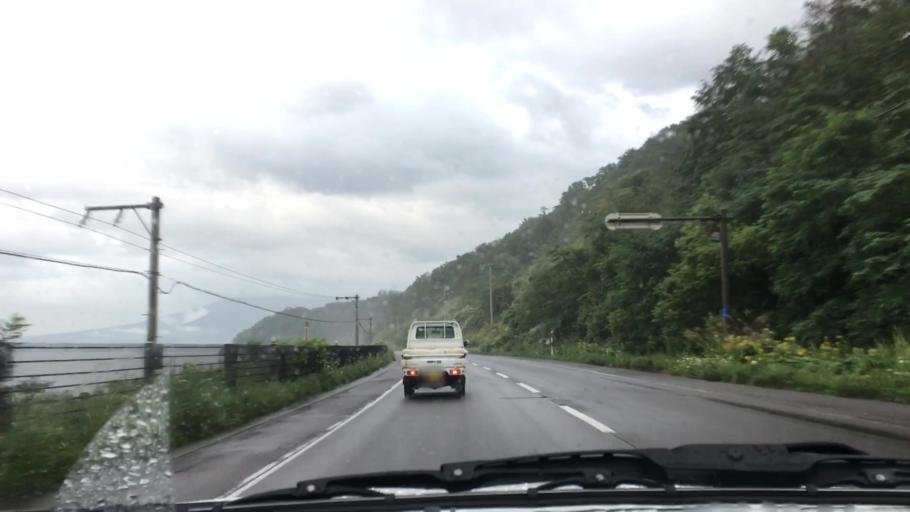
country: JP
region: Hokkaido
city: Nanae
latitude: 42.1255
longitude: 140.5197
